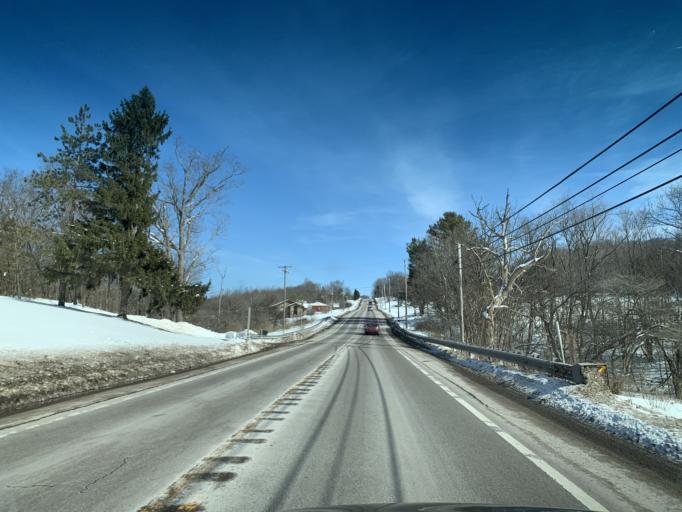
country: US
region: Pennsylvania
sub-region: Somerset County
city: Meyersdale
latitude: 39.6961
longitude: -79.1305
